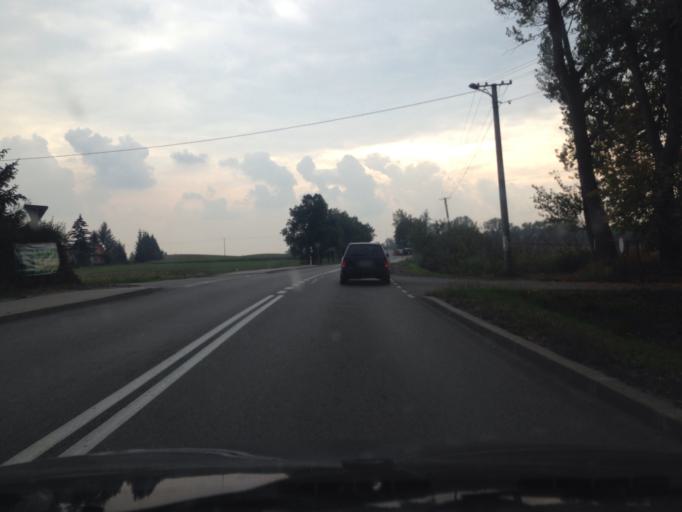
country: PL
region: Pomeranian Voivodeship
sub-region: Powiat sztumski
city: Sztum
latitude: 53.9561
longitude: 19.0235
